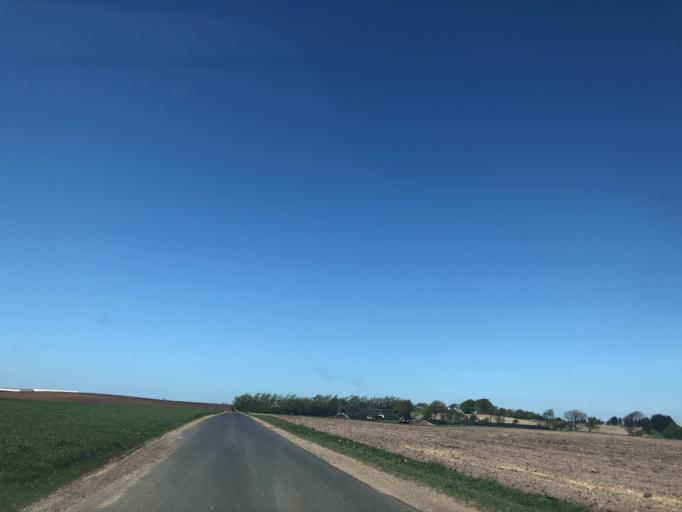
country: DK
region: Central Jutland
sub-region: Holstebro Kommune
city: Vinderup
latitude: 56.5262
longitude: 8.7780
